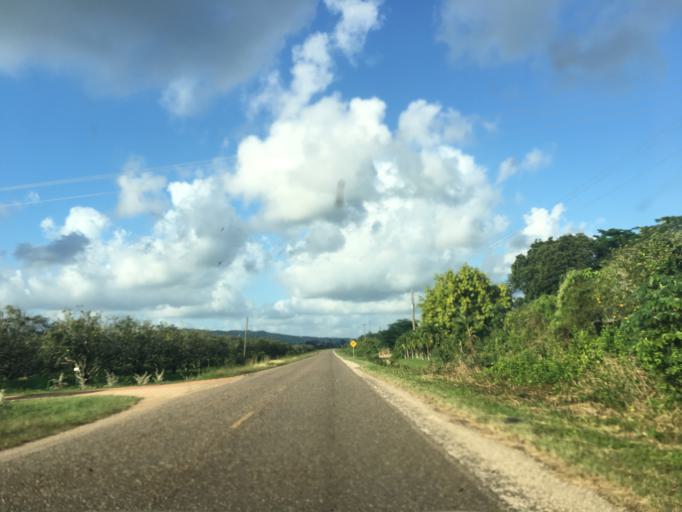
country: BZ
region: Stann Creek
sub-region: Dangriga
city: Dangriga
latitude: 16.8031
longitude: -88.3797
